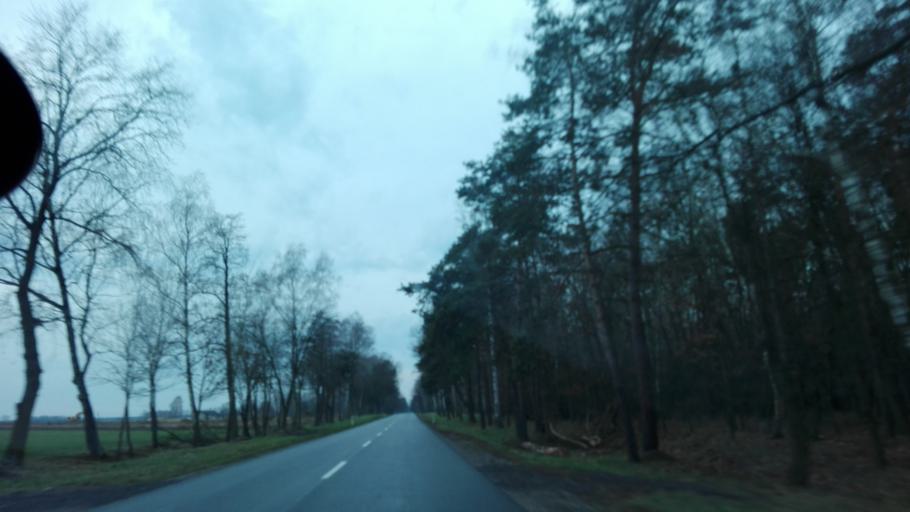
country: PL
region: Lublin Voivodeship
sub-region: Powiat radzynski
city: Wohyn
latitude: 51.7808
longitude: 22.7153
